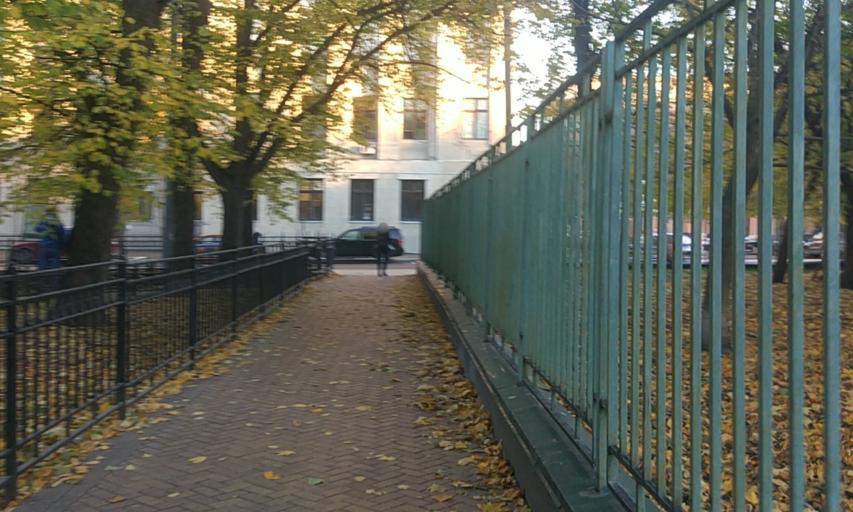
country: RU
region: Moscow
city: Mar'ina Roshcha
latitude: 55.7774
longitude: 37.5940
